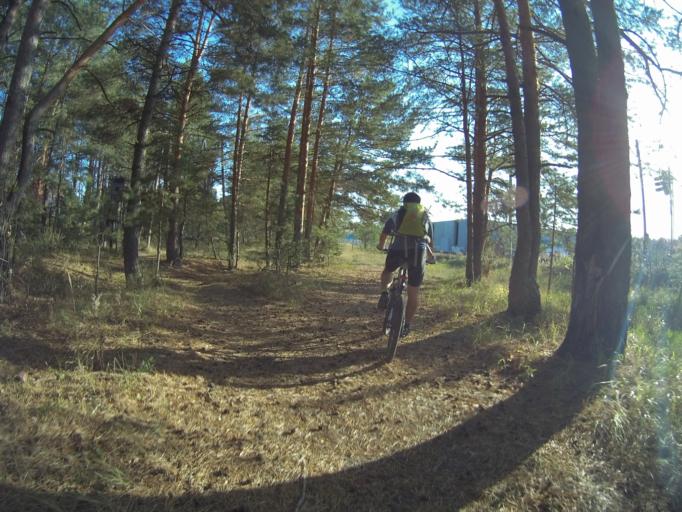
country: RU
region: Vladimir
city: Raduzhnyy
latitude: 56.0302
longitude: 40.3844
